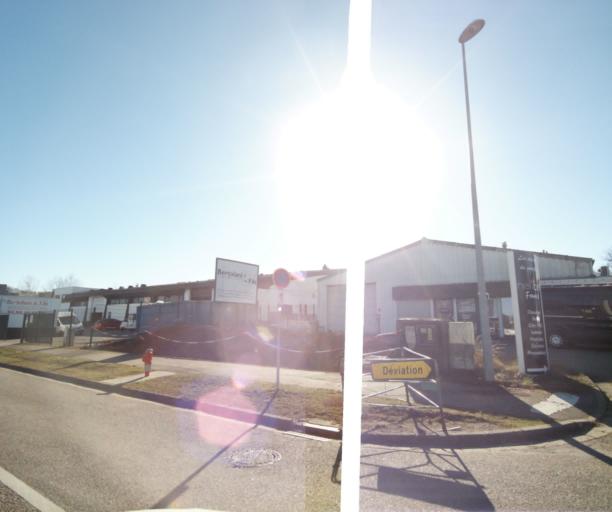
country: FR
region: Lorraine
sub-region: Departement de Meurthe-et-Moselle
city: Vandoeuvre-les-Nancy
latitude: 48.6423
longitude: 6.1874
